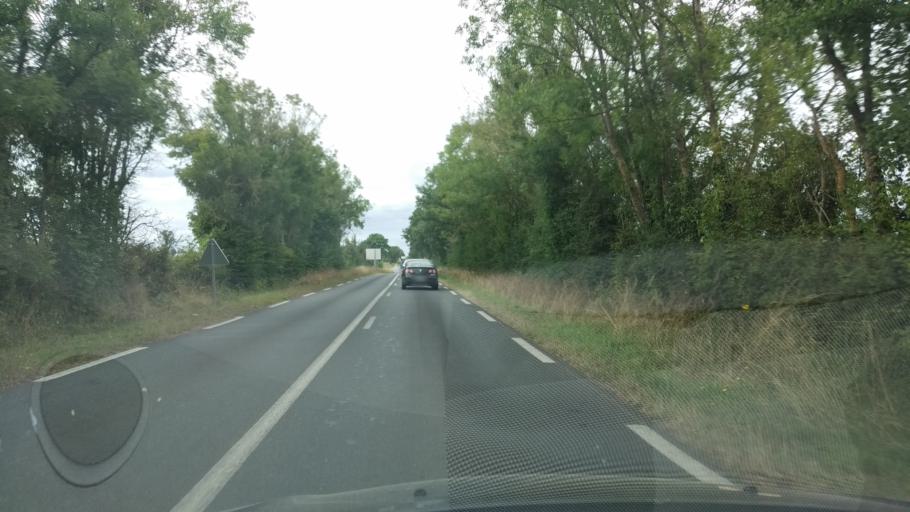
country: FR
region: Poitou-Charentes
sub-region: Departement de la Vienne
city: Roches-Premarie-Andille
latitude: 46.4959
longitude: 0.3655
